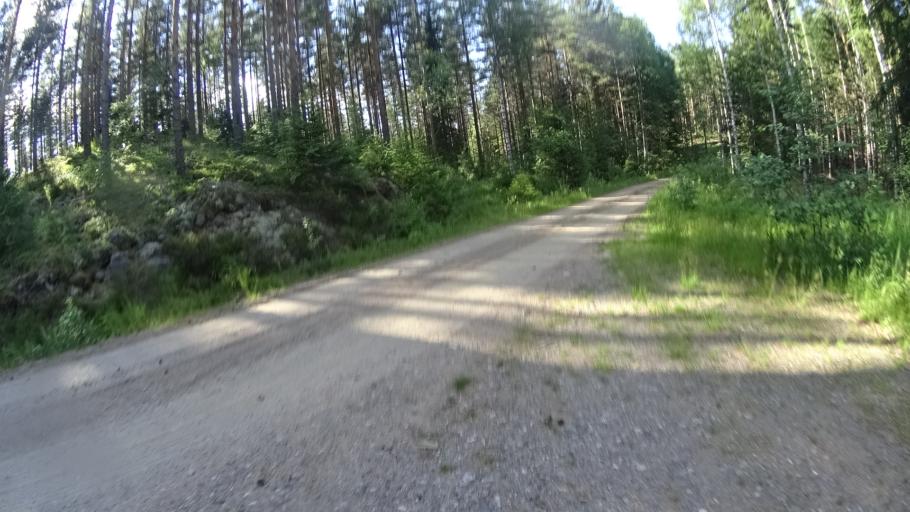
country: FI
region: Uusimaa
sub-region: Helsinki
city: Karkkila
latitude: 60.6391
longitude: 24.1619
